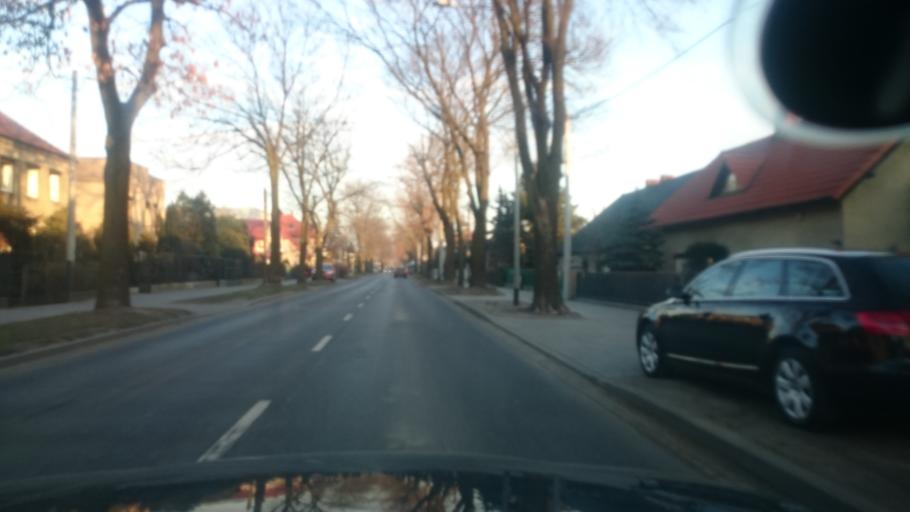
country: PL
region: Greater Poland Voivodeship
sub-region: Powiat ostrowski
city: Ostrow Wielkopolski
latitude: 51.6489
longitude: 17.8421
